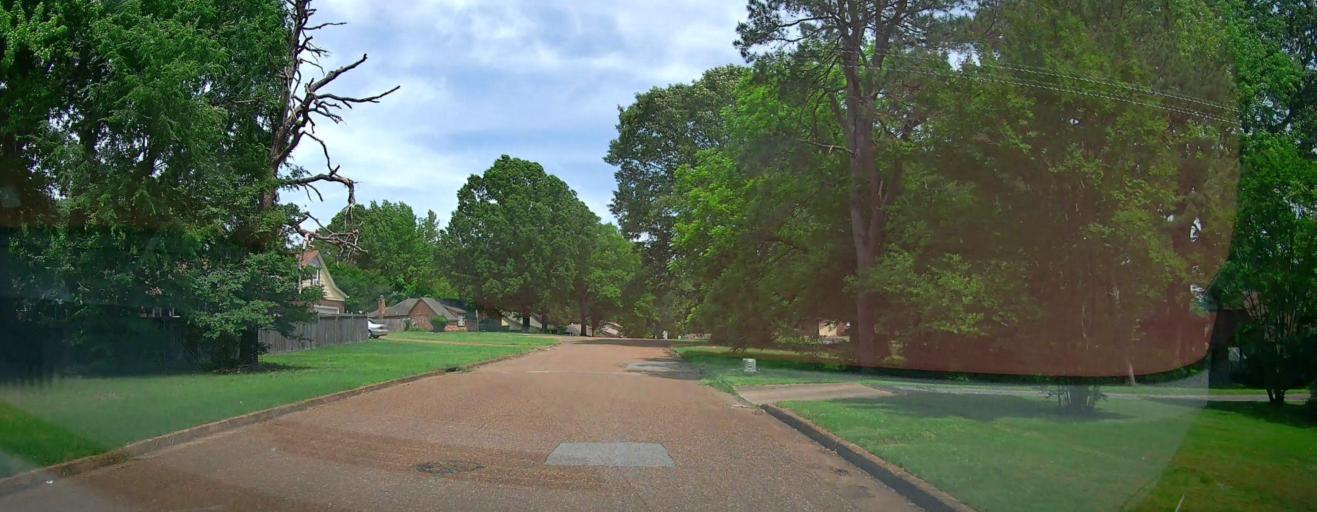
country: US
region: Tennessee
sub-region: Shelby County
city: Germantown
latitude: 35.0440
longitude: -89.7903
